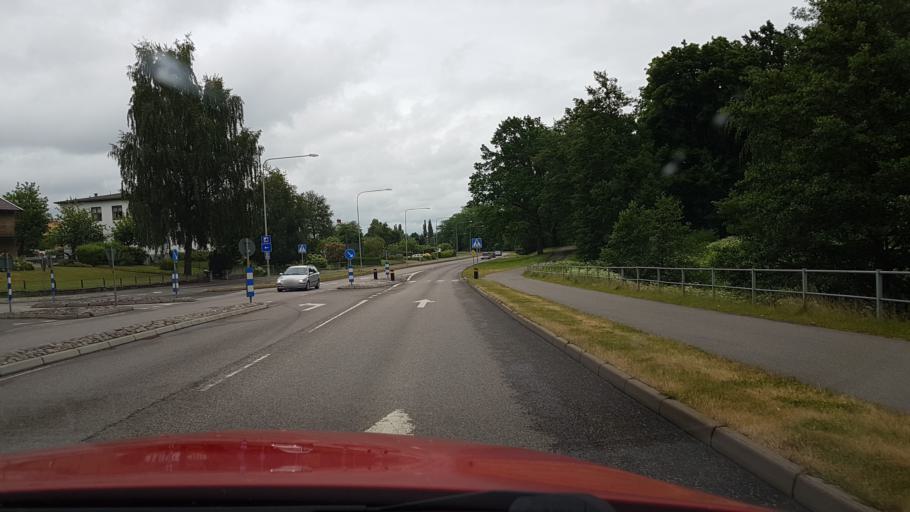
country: SE
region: Vaestra Goetaland
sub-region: Skovde Kommun
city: Skoevde
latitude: 58.3922
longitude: 13.8567
